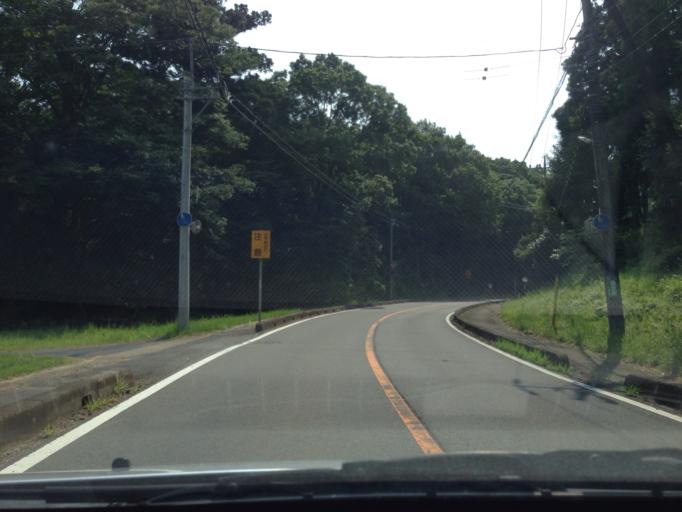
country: JP
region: Ibaraki
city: Inashiki
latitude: 36.0113
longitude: 140.3445
